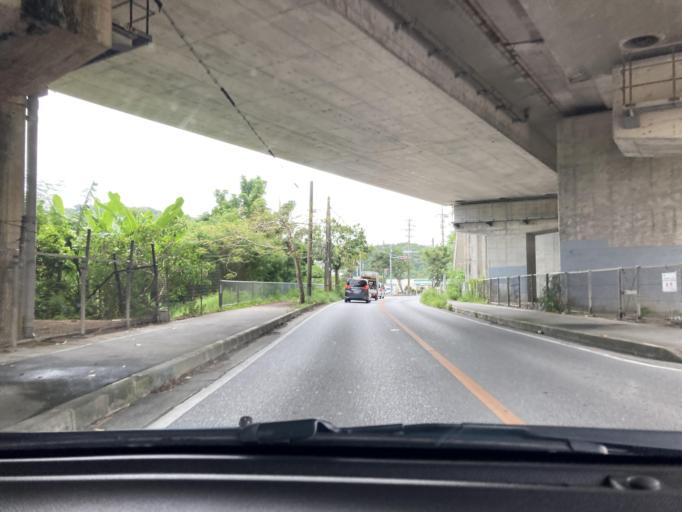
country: JP
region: Okinawa
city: Ginowan
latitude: 26.2800
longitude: 127.7844
